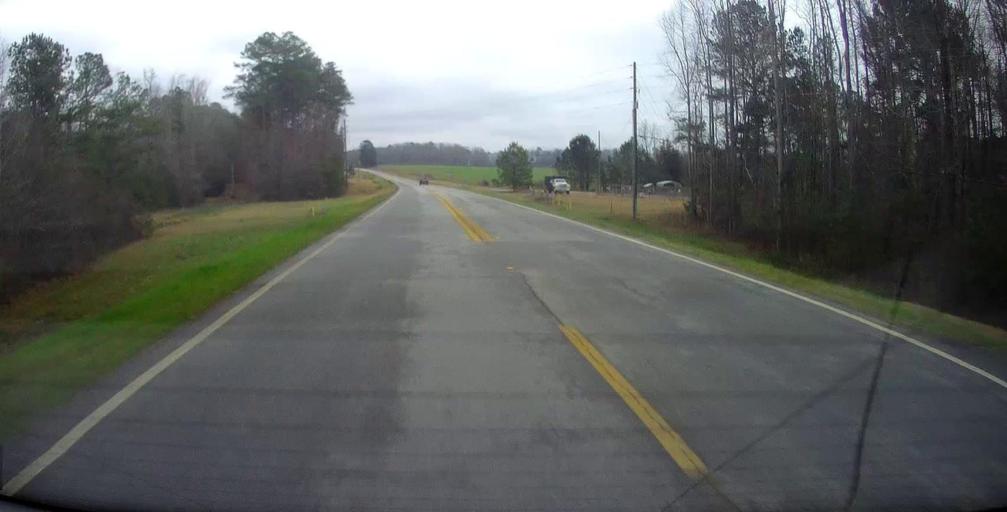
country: US
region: Georgia
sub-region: Lamar County
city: Barnesville
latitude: 33.0668
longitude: -84.2283
